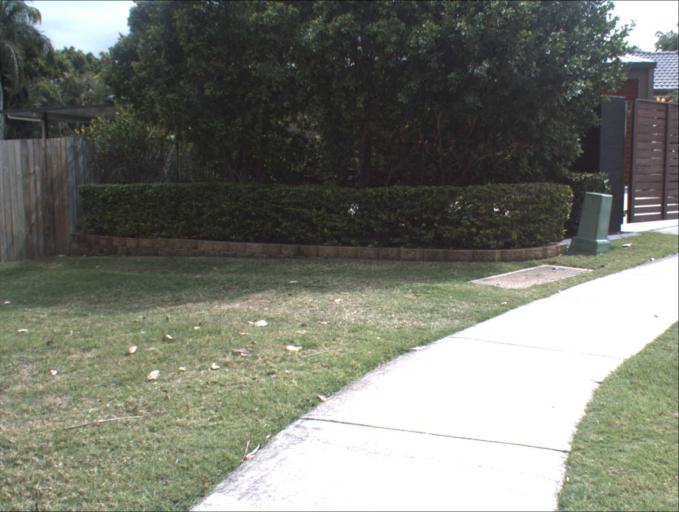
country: AU
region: Queensland
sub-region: Logan
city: Logan Reserve
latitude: -27.6880
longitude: 153.0615
